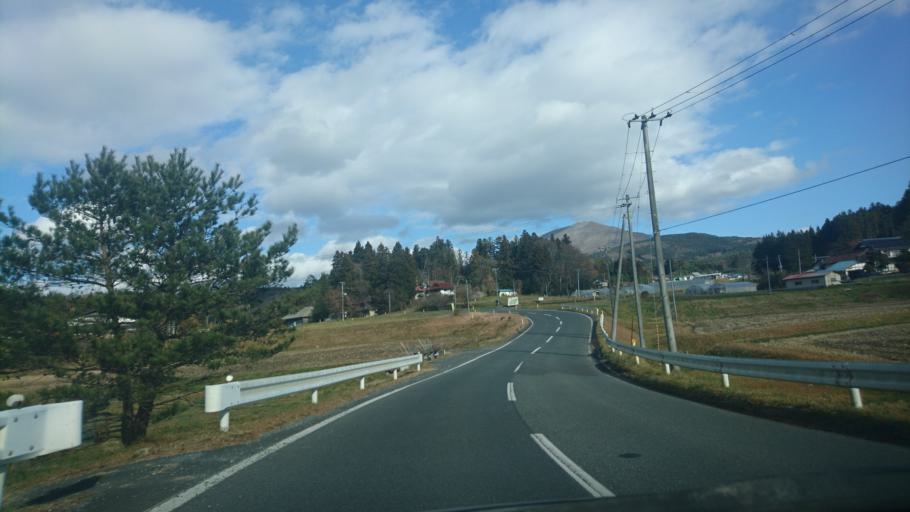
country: JP
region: Iwate
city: Ichinoseki
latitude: 38.9461
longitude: 141.4064
